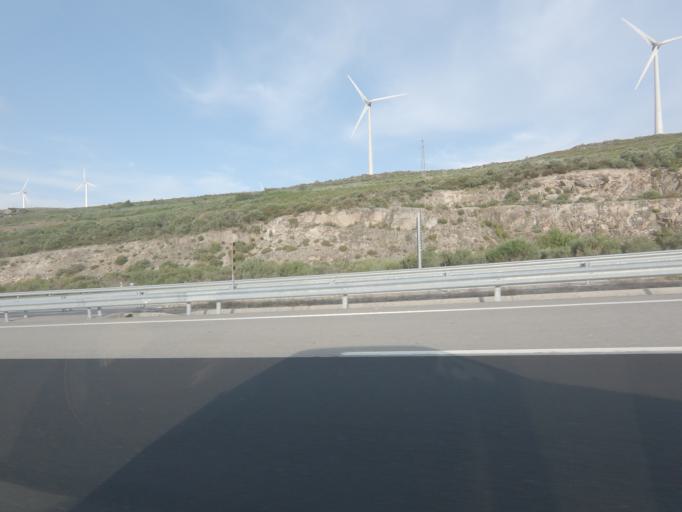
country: PT
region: Vila Real
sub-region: Vila Pouca de Aguiar
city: Vila Pouca de Aguiar
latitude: 41.4517
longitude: -7.6465
